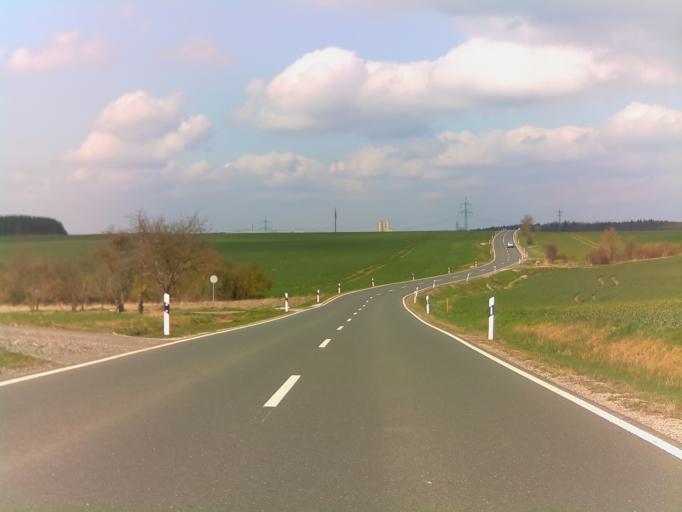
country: DE
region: Thuringia
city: Milda
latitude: 50.8652
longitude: 11.4569
